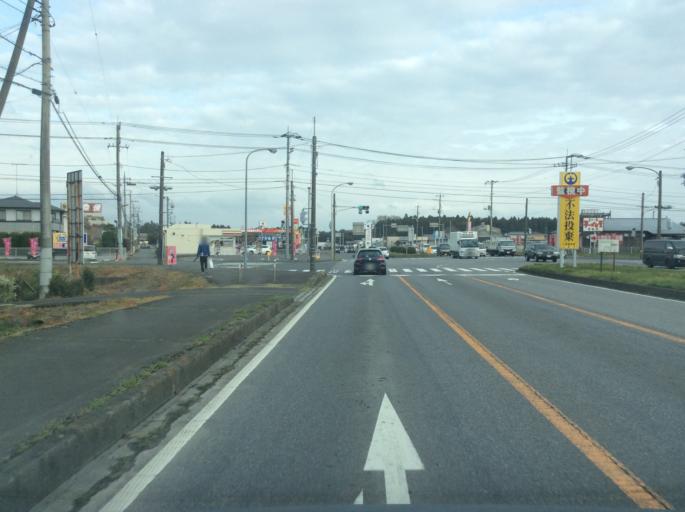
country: JP
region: Ibaraki
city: Naka
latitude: 36.1201
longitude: 140.1786
